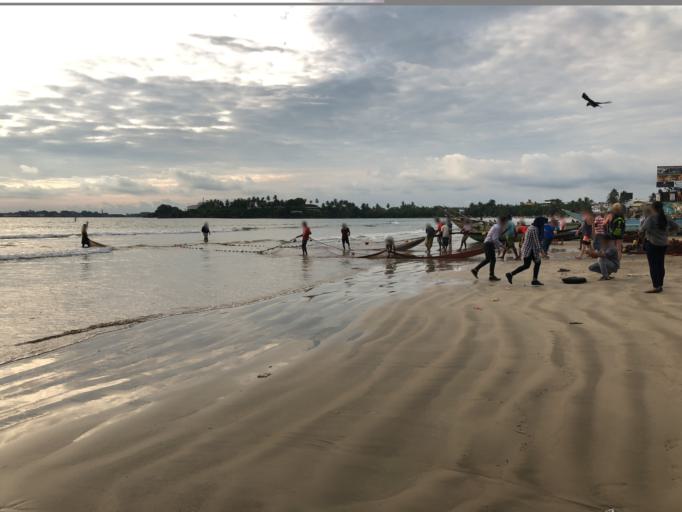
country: LK
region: Southern
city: Unawatuna
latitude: 6.0293
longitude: 80.2417
